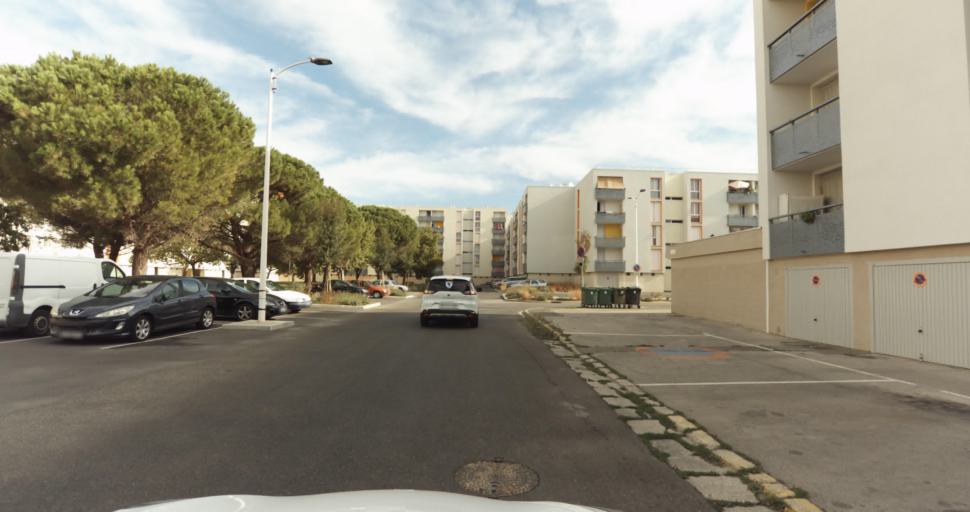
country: FR
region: Provence-Alpes-Cote d'Azur
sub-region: Departement des Bouches-du-Rhone
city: Miramas
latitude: 43.5902
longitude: 5.0055
